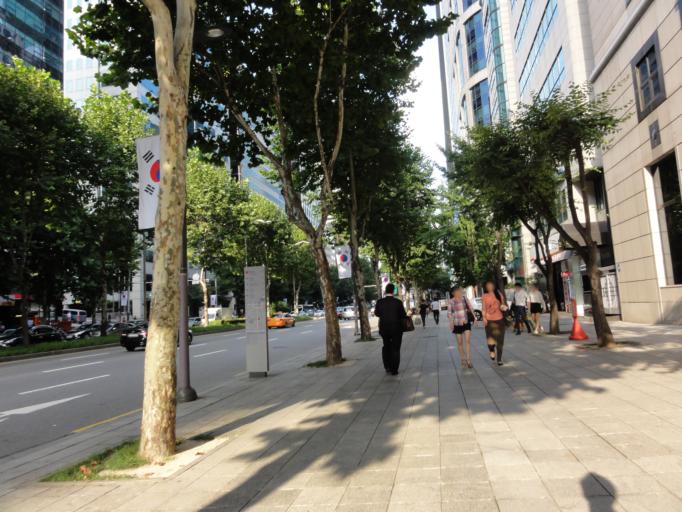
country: KR
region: Seoul
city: Seoul
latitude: 37.4989
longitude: 127.0327
